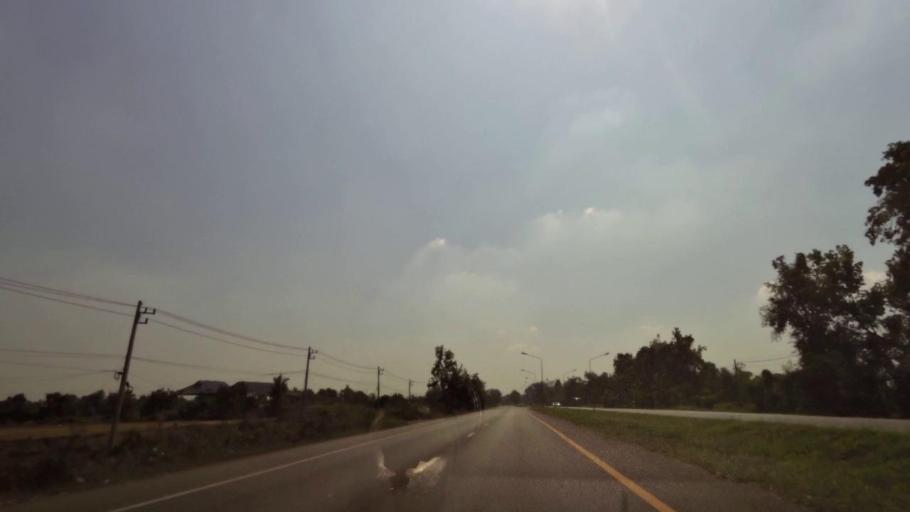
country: TH
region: Phichit
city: Bueng Na Rang
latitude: 16.2450
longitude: 100.1255
